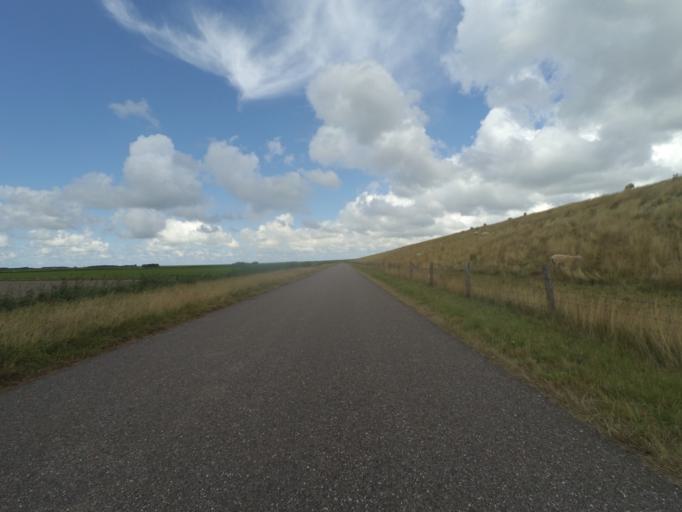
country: NL
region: North Holland
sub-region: Gemeente Texel
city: Den Burg
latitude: 53.1348
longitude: 4.9006
